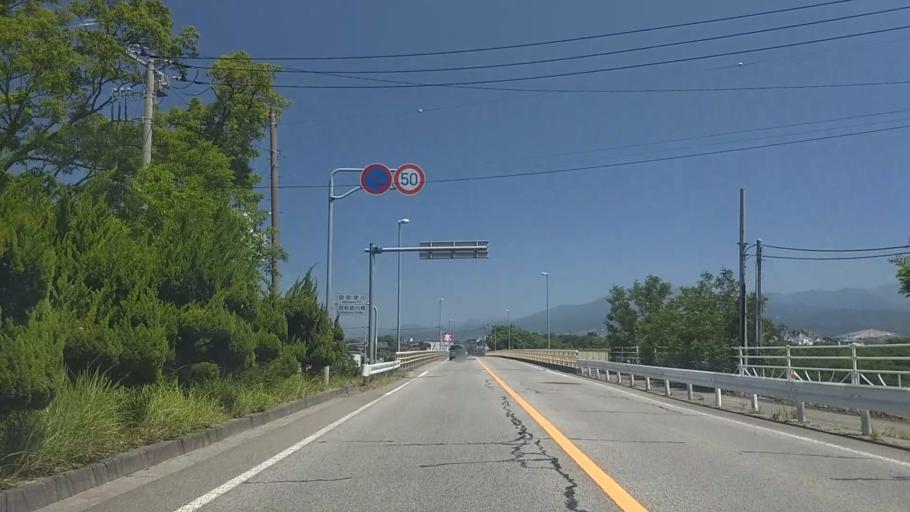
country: JP
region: Yamanashi
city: Nirasaki
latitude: 35.6706
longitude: 138.4648
